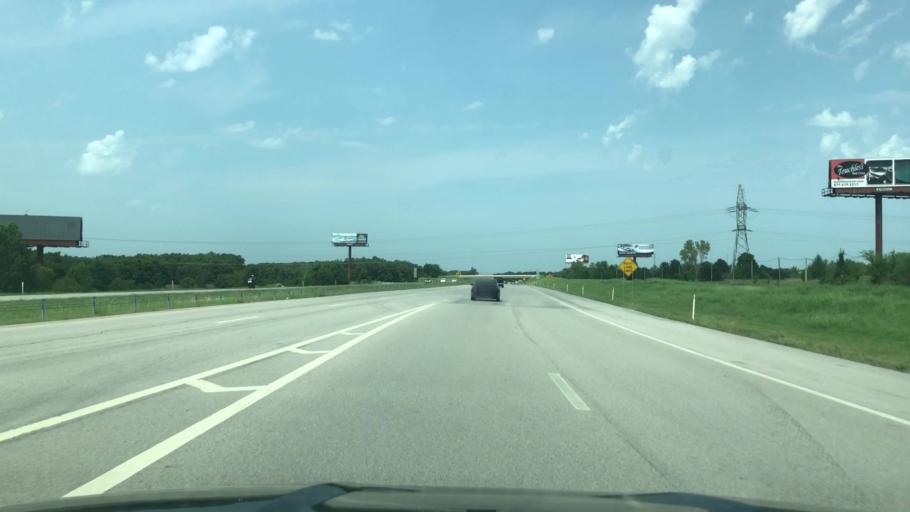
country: US
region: Oklahoma
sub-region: Rogers County
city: Catoosa
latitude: 36.1699
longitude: -95.7319
